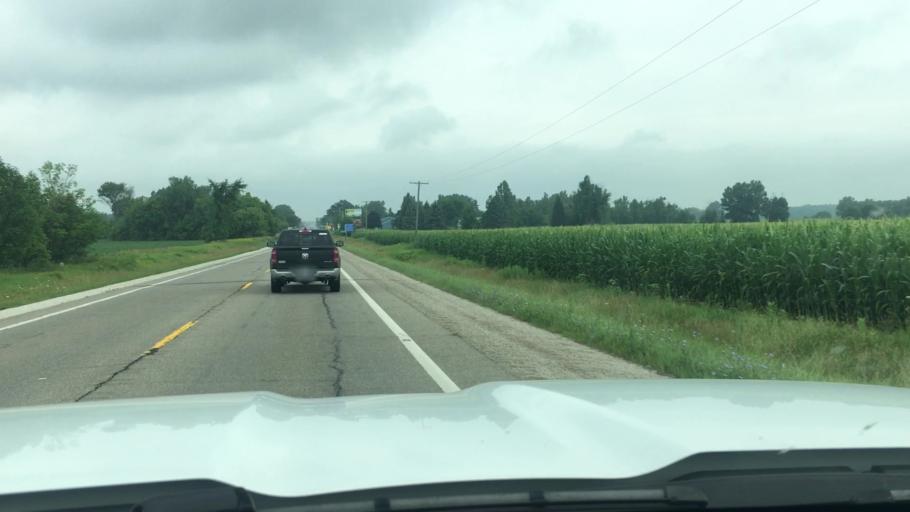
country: US
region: Michigan
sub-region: Sanilac County
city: Brown City
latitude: 43.2042
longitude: -83.0771
